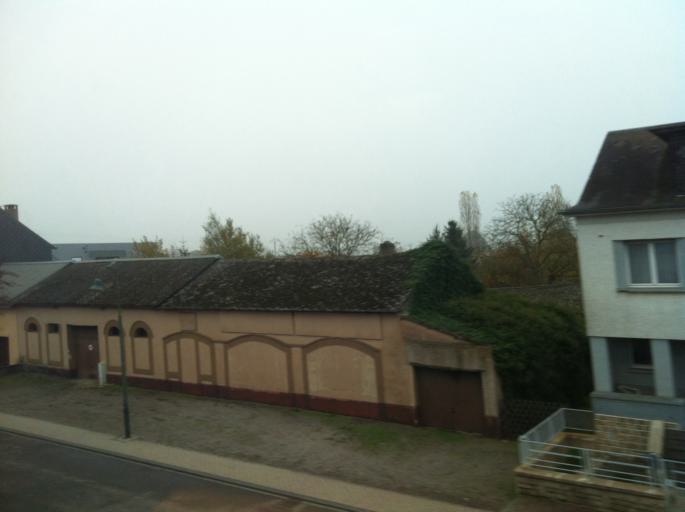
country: LU
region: Luxembourg
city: Crauthem
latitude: 49.5414
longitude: 6.1328
